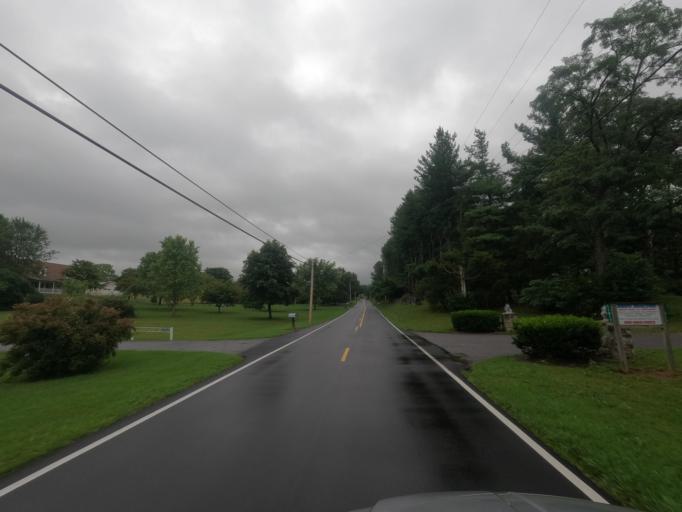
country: US
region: Maryland
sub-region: Washington County
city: Wilson-Conococheague
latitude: 39.6386
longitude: -77.9340
